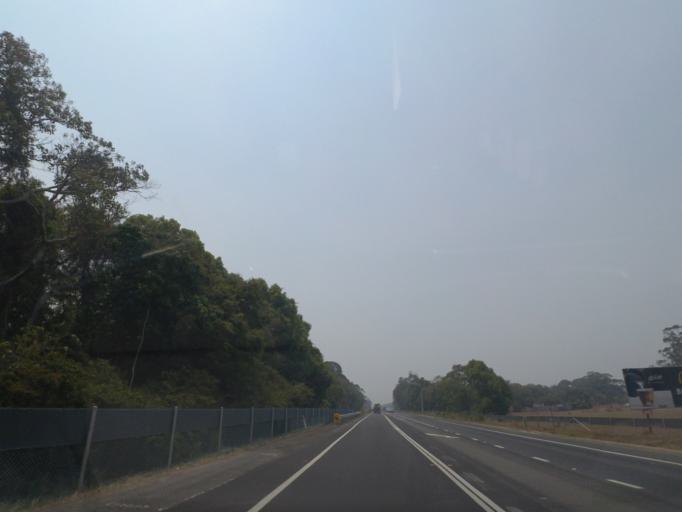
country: AU
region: New South Wales
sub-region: Ballina
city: Ballina
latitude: -28.9200
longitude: 153.4764
